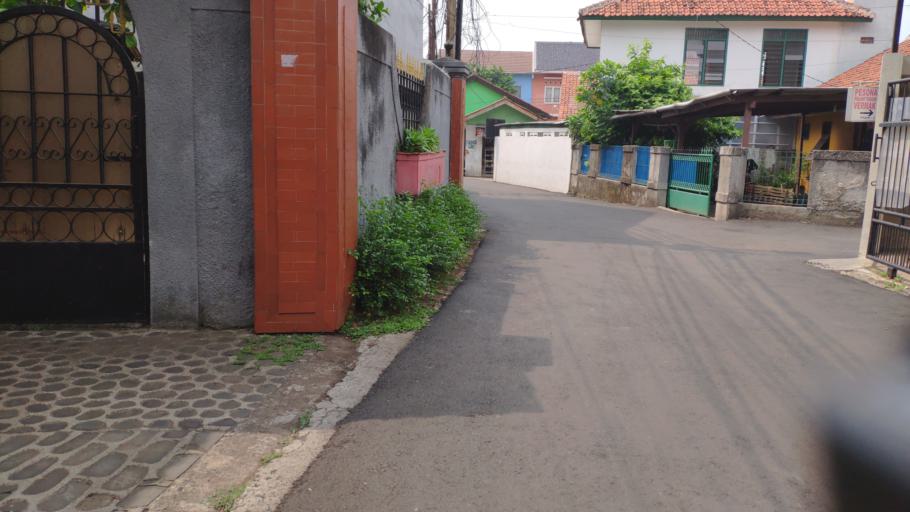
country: ID
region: West Java
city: Depok
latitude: -6.3206
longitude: 106.8213
